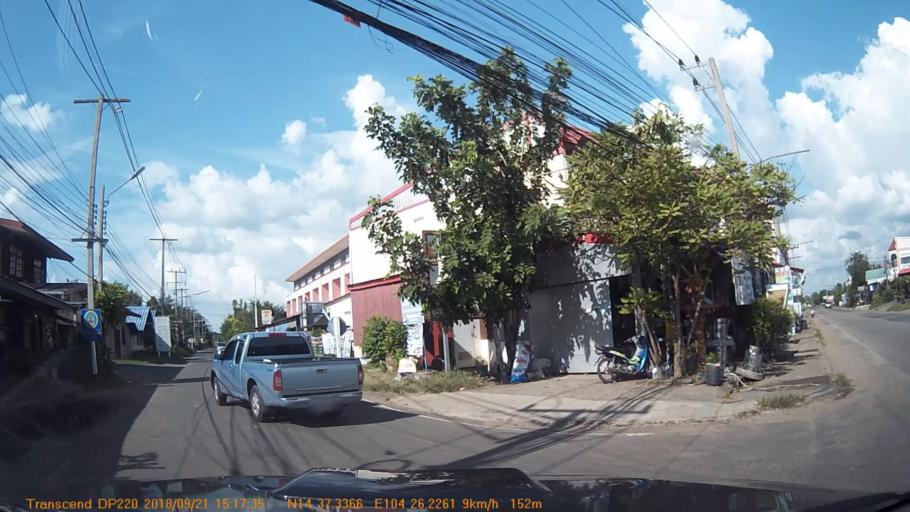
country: TH
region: Sisaket
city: Khun Han
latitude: 14.6224
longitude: 104.4371
